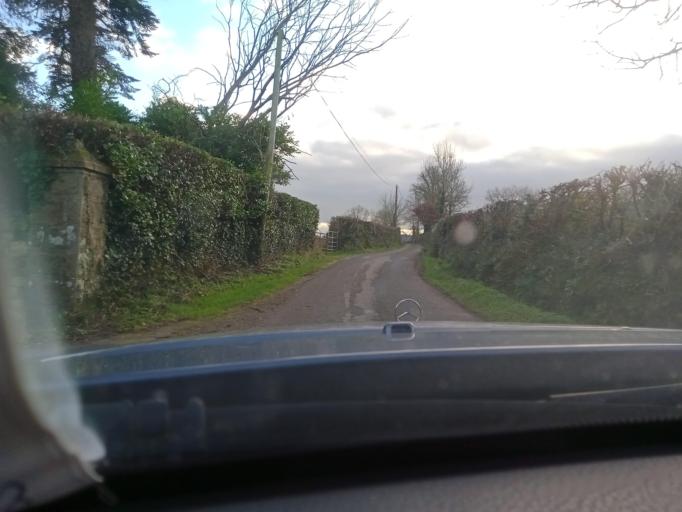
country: IE
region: Leinster
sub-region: Kilkenny
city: Graiguenamanagh
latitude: 52.5092
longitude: -6.9412
